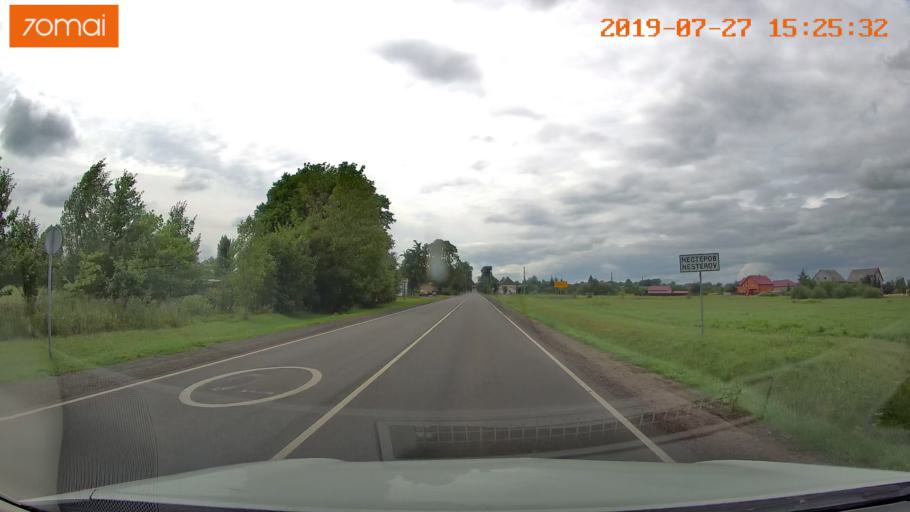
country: RU
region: Kaliningrad
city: Nesterov
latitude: 54.6318
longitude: 22.5881
